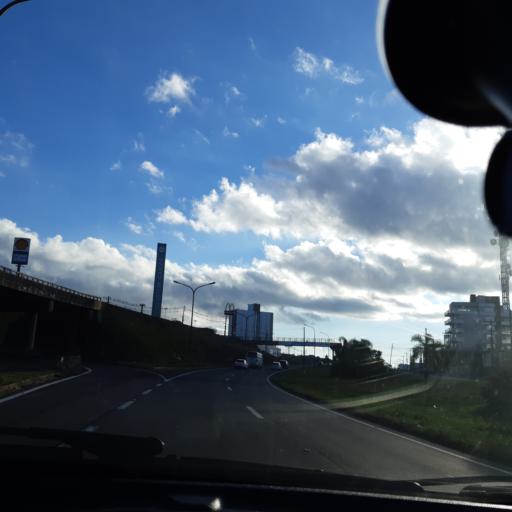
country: BR
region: Rio Grande do Sul
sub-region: Caxias Do Sul
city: Caxias do Sul
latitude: -29.1755
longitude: -51.2157
